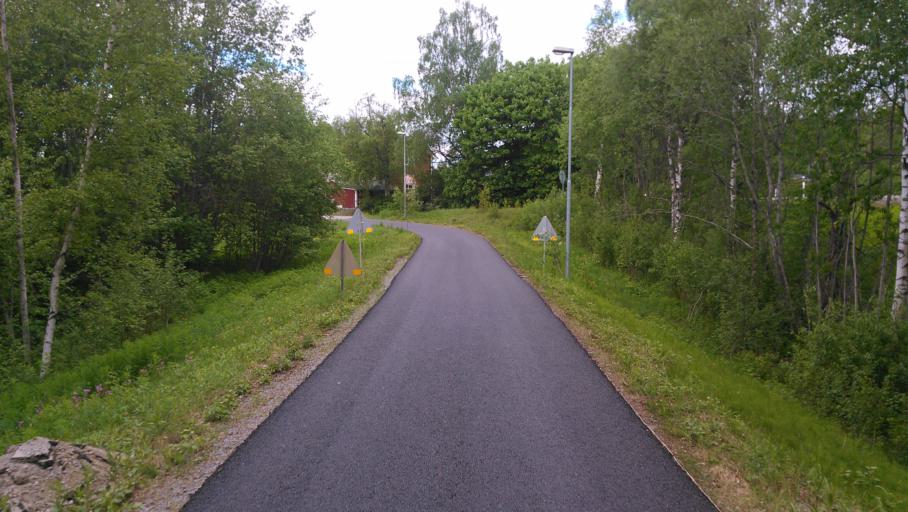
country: SE
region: Vaesterbotten
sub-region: Umea Kommun
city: Roback
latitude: 63.8574
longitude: 20.0935
